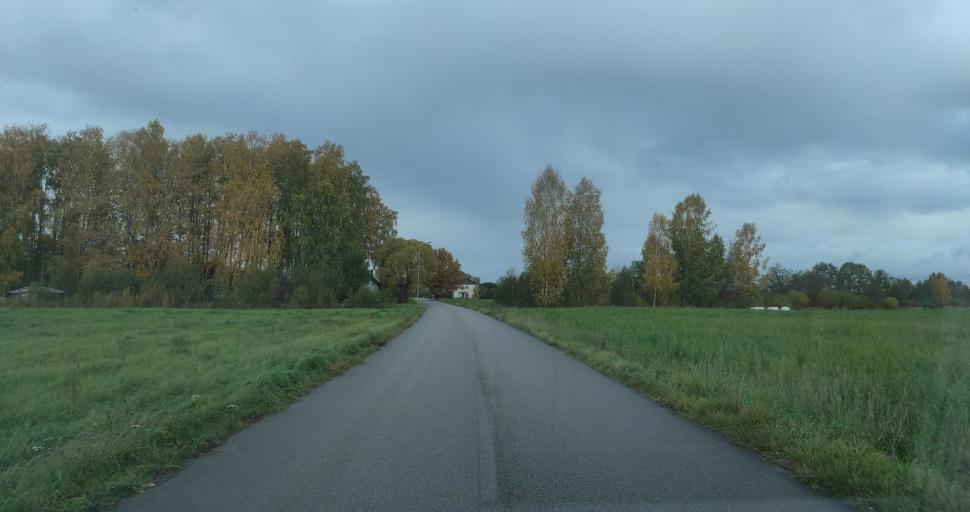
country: LV
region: Skrunda
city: Skrunda
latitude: 56.6928
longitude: 22.0162
